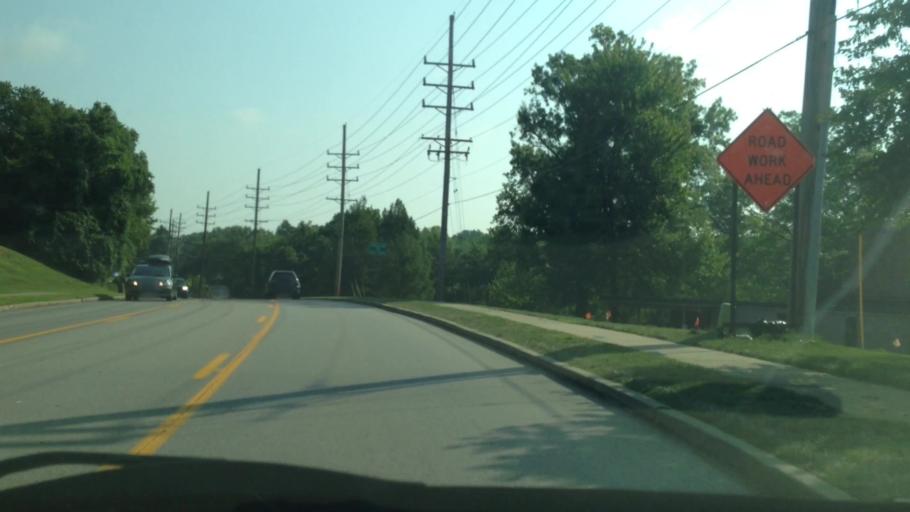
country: US
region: Missouri
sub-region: Saint Louis County
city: Des Peres
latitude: 38.5825
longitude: -90.4454
